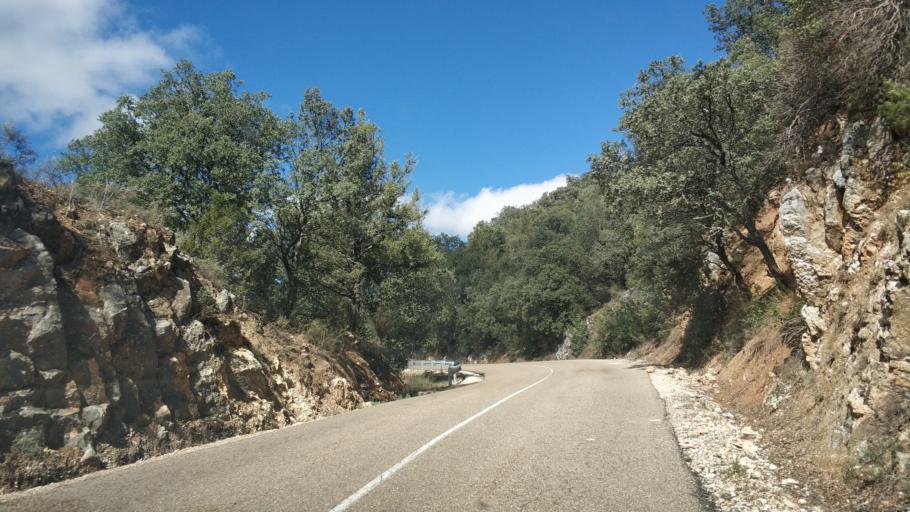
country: ES
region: Castille and Leon
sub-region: Provincia de Burgos
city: Retuerta
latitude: 42.0464
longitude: -3.4699
